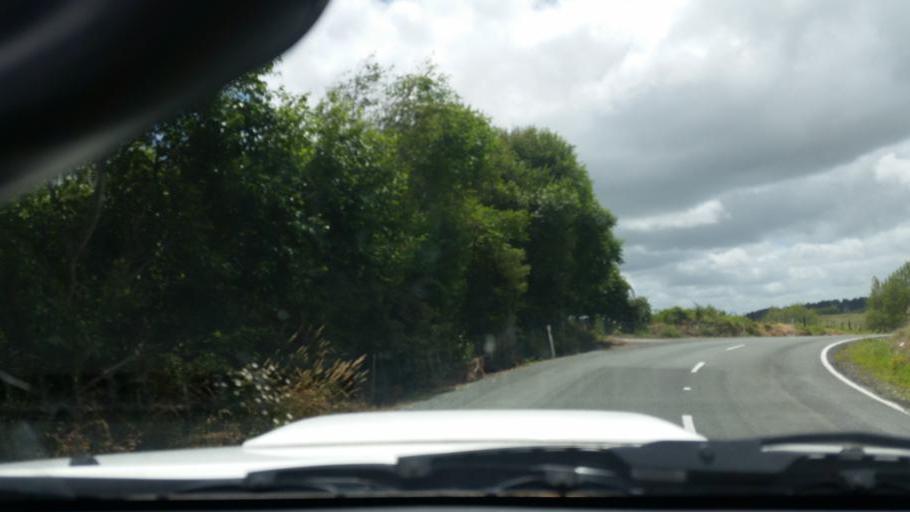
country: NZ
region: Auckland
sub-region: Auckland
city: Wellsford
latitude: -36.1262
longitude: 174.3280
